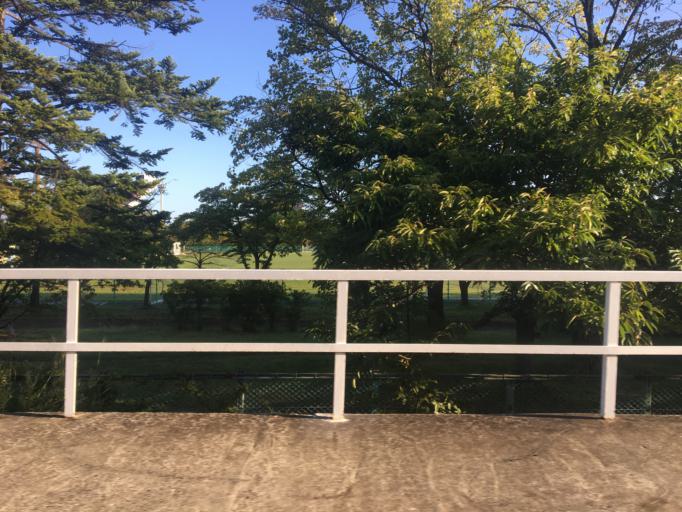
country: JP
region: Aomori
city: Hirosaki
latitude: 40.5896
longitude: 140.5029
